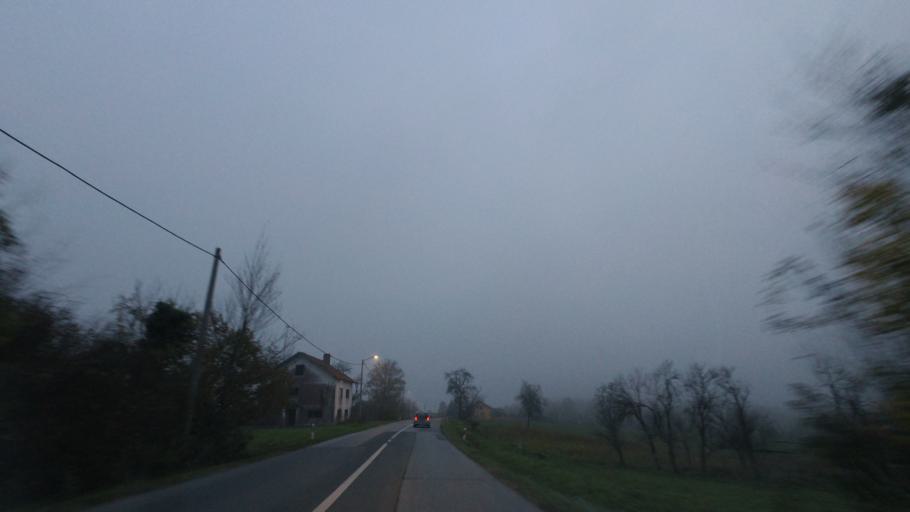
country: HR
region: Sisacko-Moslavacka
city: Glina
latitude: 45.4077
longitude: 16.1734
